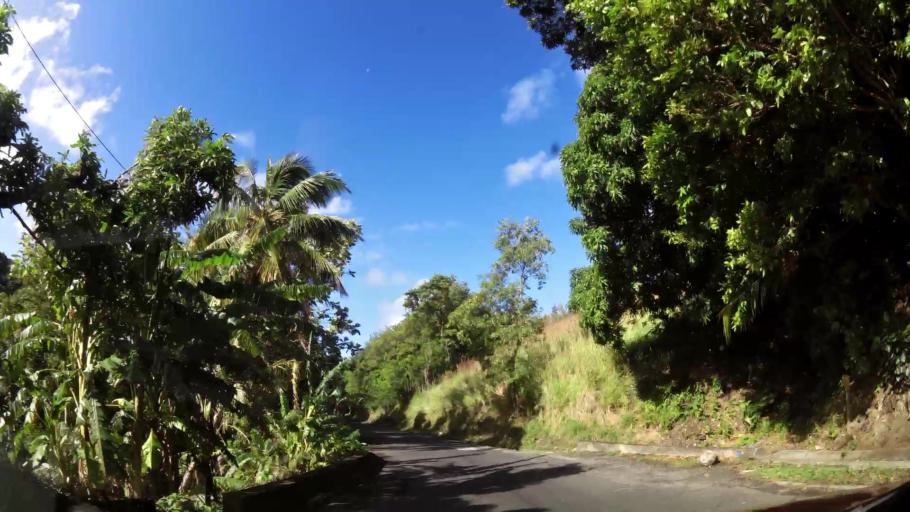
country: DM
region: Saint John
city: Portsmouth
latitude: 15.5740
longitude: -61.4376
